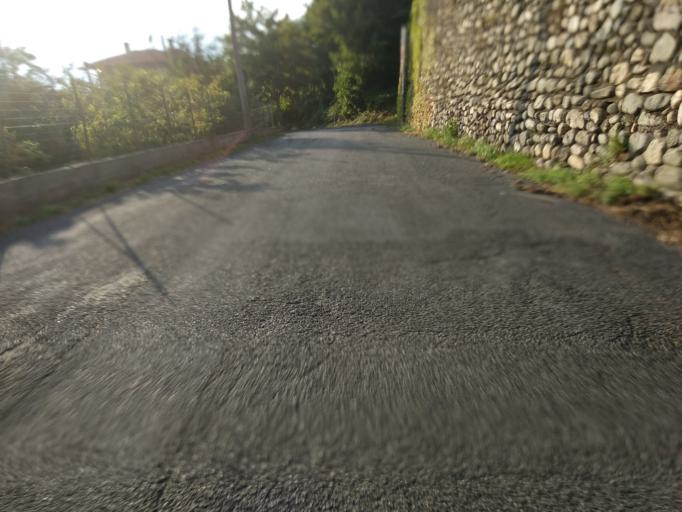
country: IT
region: Piedmont
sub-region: Provincia di Cuneo
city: Garessio
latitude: 44.1987
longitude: 8.0318
